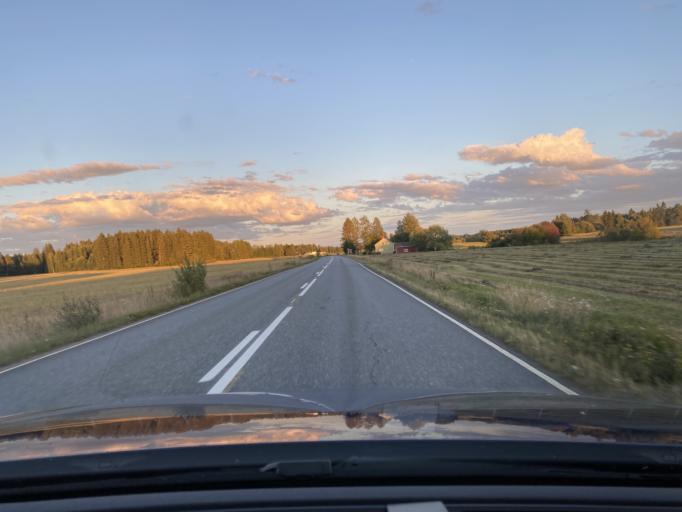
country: FI
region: Satakunta
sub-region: Pori
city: Huittinen
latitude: 61.1523
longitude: 22.8268
